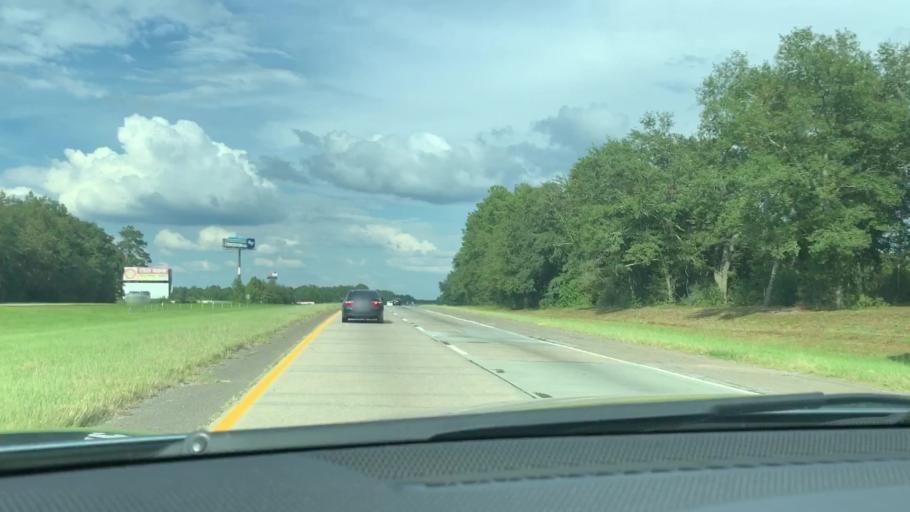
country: US
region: South Carolina
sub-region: Hampton County
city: Yemassee
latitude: 32.6945
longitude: -80.8782
